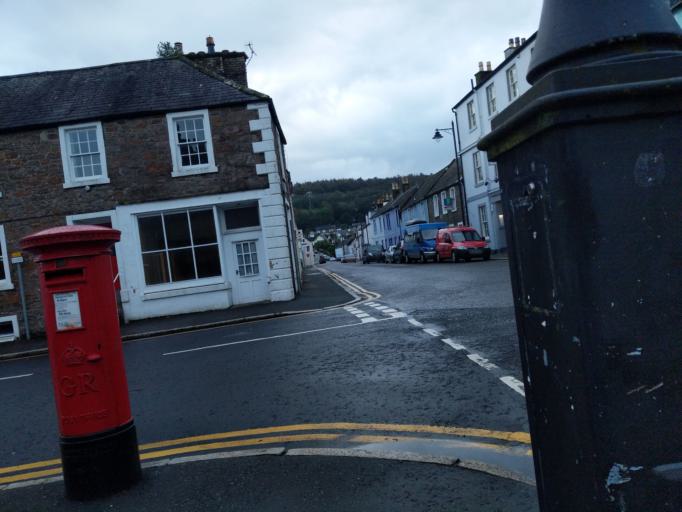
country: GB
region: Scotland
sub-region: Dumfries and Galloway
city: Kirkcudbright
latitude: 54.8351
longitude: -4.0539
